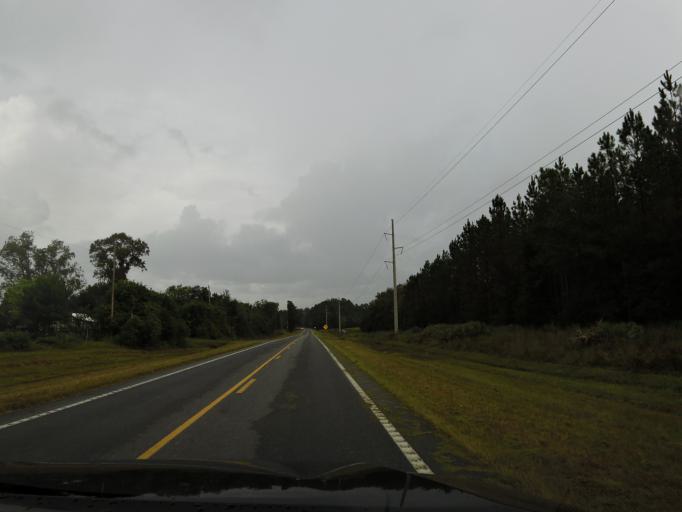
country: US
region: Florida
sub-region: Duval County
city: Baldwin
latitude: 30.5008
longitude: -82.0371
